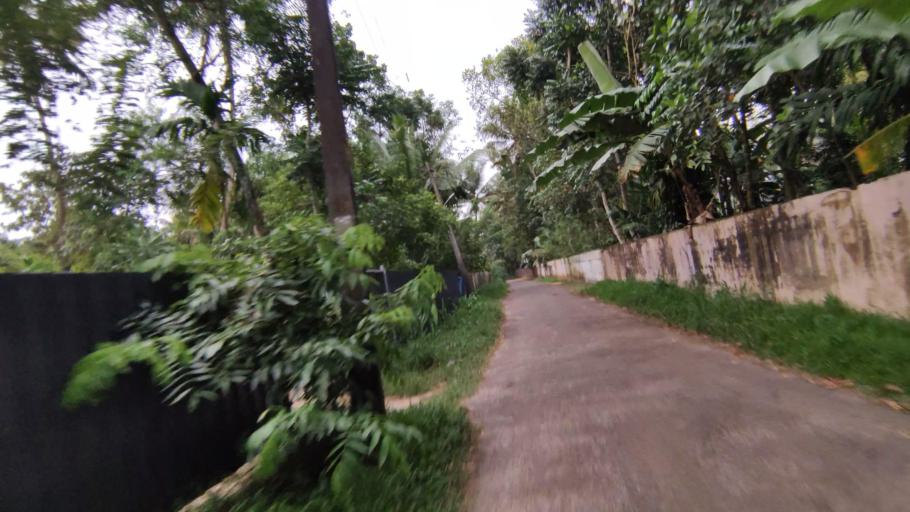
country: IN
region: Kerala
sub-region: Alappuzha
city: Shertallai
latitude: 9.6397
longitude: 76.3629
